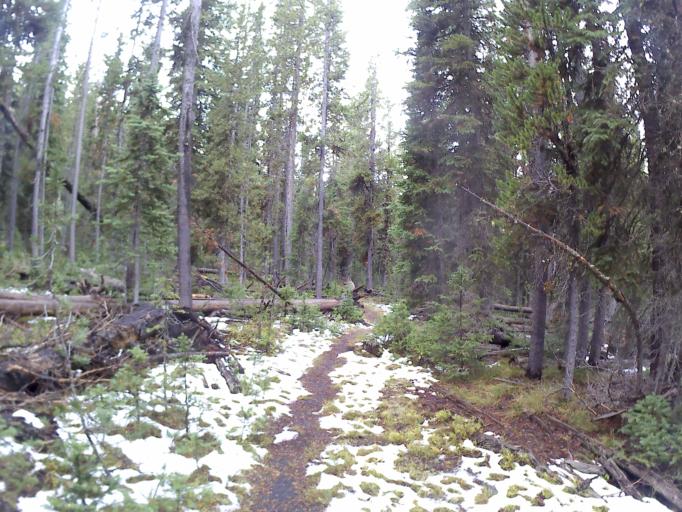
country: US
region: Montana
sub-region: Gallatin County
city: West Yellowstone
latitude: 44.4331
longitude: -110.7327
